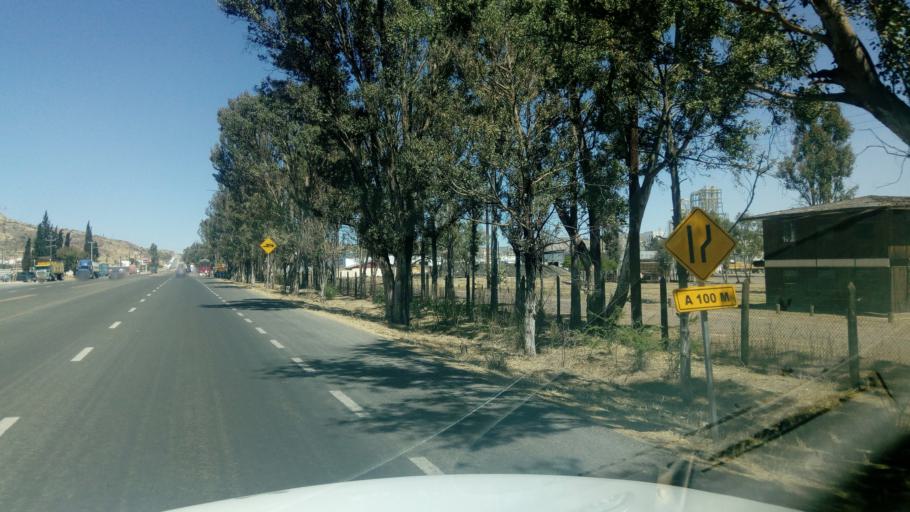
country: MX
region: Durango
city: Victoria de Durango
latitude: 24.0764
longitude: -104.6638
